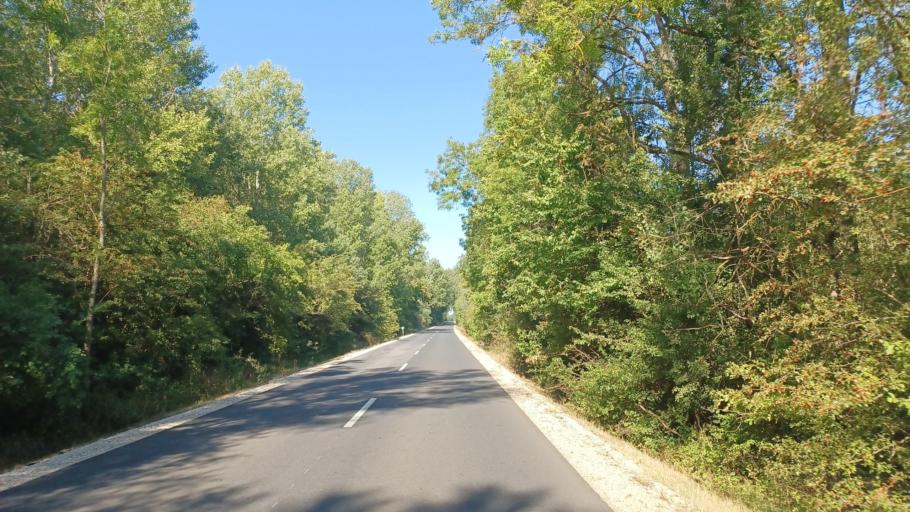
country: HU
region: Tolna
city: Nemetker
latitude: 46.7327
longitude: 18.7244
